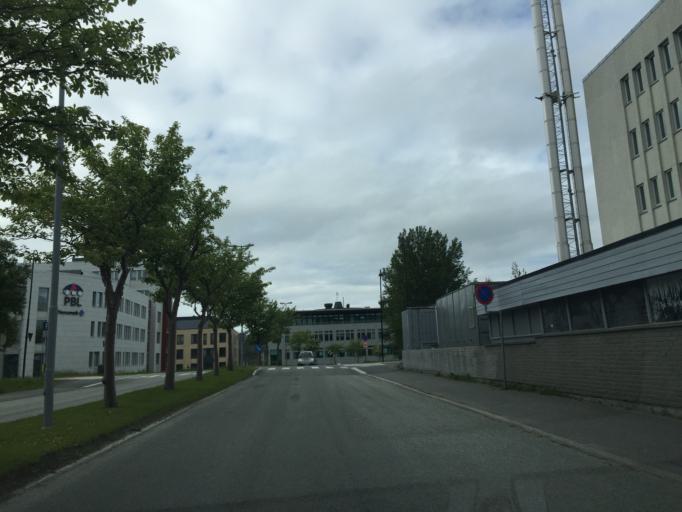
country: NO
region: Nordland
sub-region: Bodo
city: Bodo
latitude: 67.2799
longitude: 14.3757
